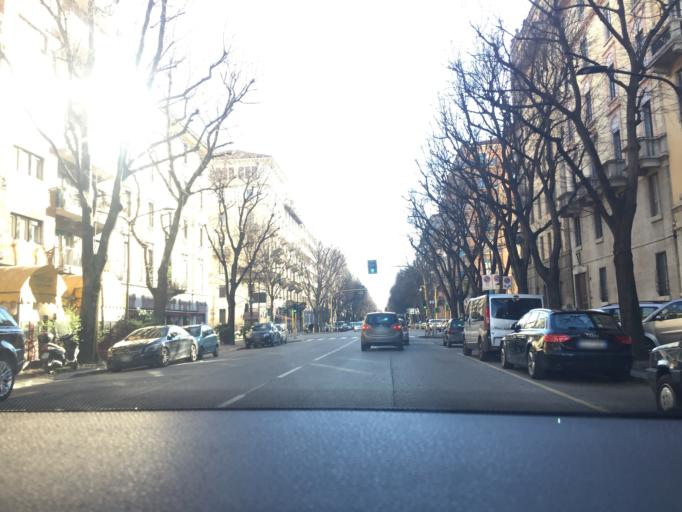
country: IT
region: Lombardy
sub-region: Citta metropolitana di Milano
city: Milano
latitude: 45.4911
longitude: 9.1665
